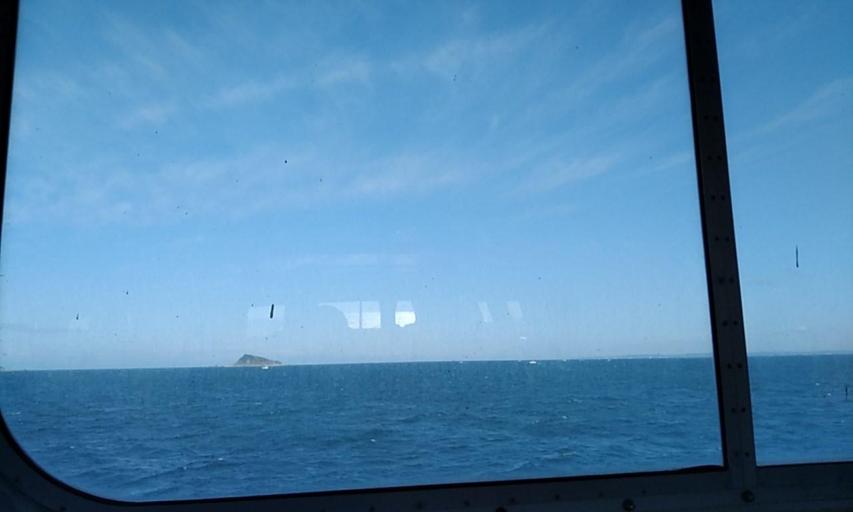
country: JP
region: Mie
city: Toba
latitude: 34.5319
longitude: 136.9469
